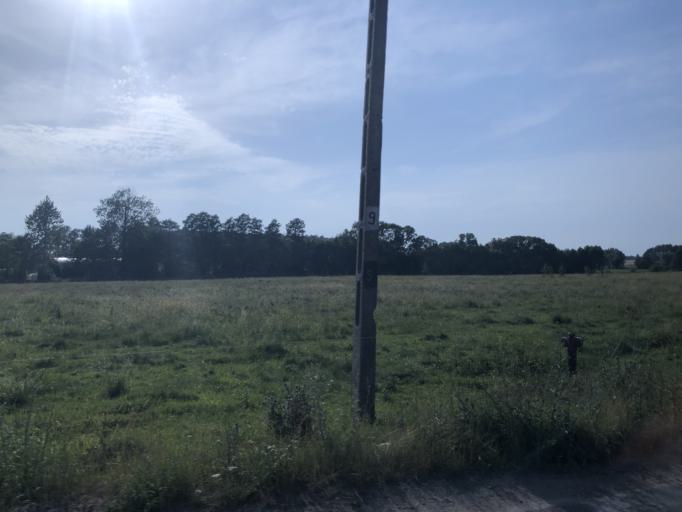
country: PL
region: Podlasie
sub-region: Lomza
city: Lomza
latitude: 53.1447
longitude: 22.0158
